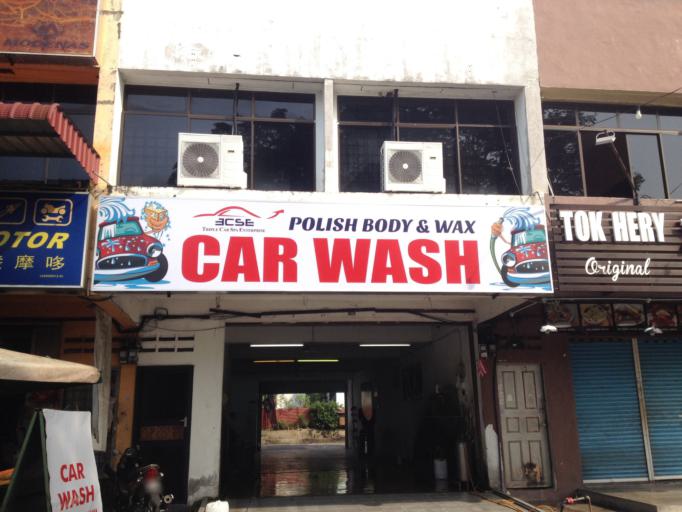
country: MY
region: Kedah
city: Kulim
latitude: 5.3793
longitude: 100.5429
